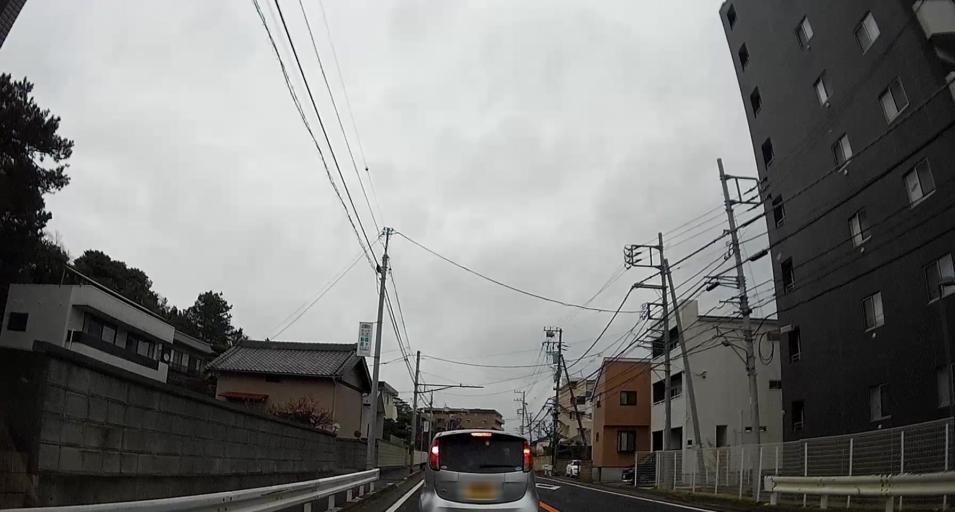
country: JP
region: Chiba
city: Funabashi
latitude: 35.7071
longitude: 139.9641
